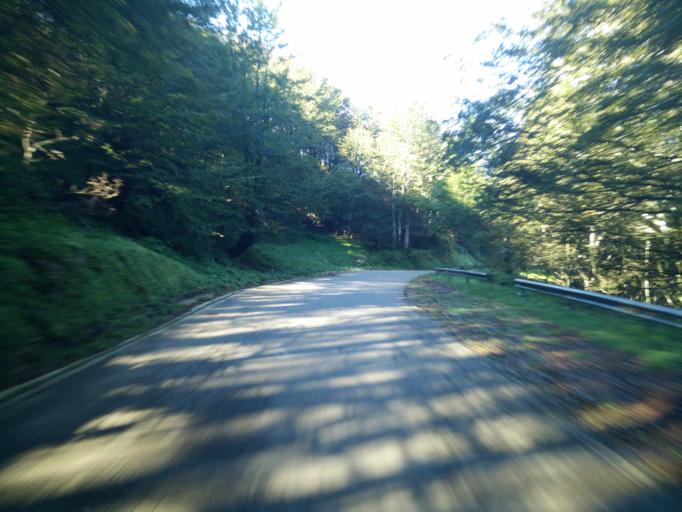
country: ES
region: Cantabria
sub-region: Provincia de Cantabria
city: San Pedro del Romeral
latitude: 43.0401
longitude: -3.8523
